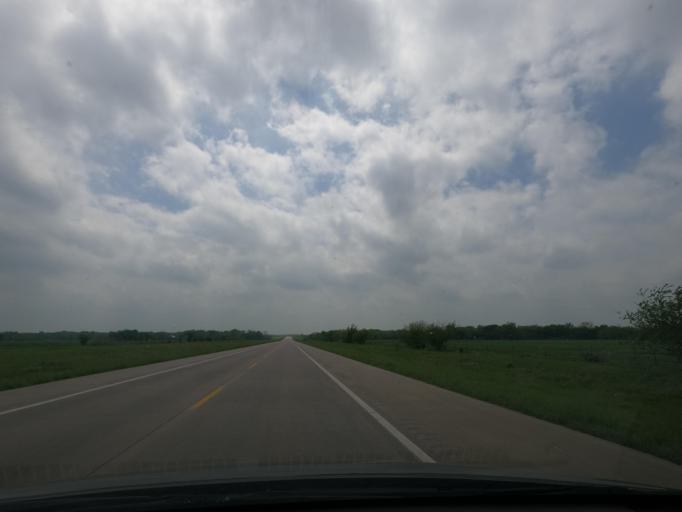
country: US
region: Kansas
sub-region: Labette County
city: Parsons
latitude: 37.3588
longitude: -95.3088
